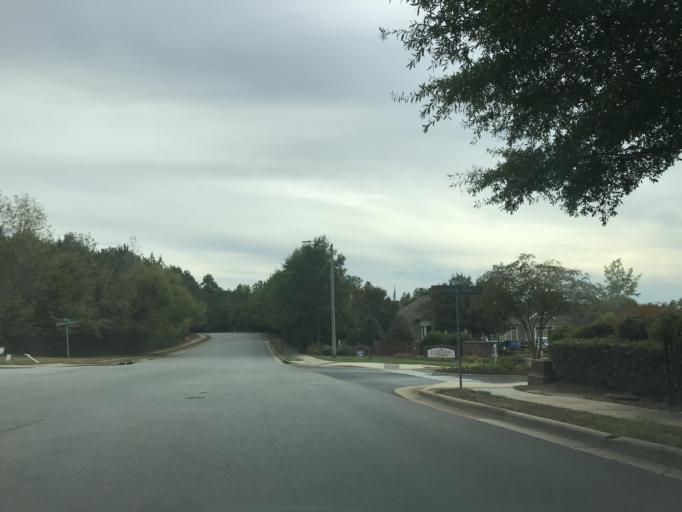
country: US
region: North Carolina
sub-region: Wake County
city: Wake Forest
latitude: 35.9448
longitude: -78.5483
